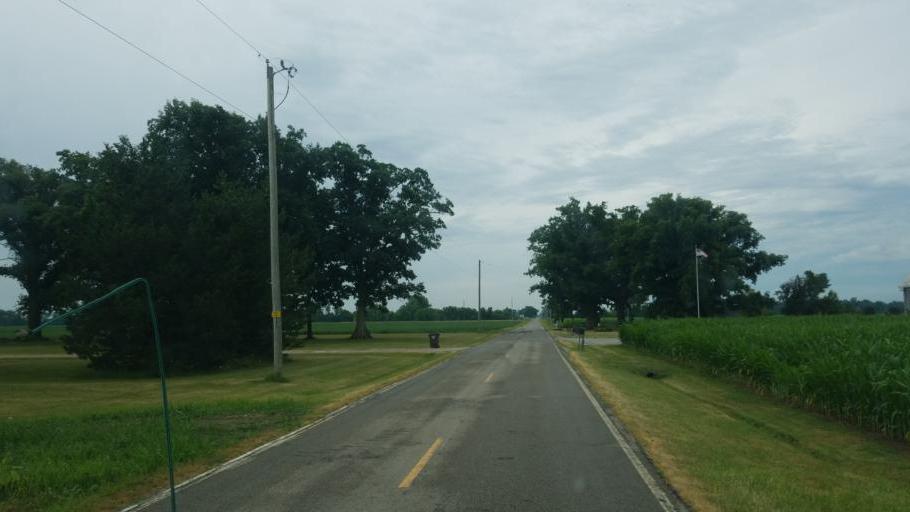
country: US
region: Ohio
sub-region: Defiance County
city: Hicksville
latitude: 41.2859
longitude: -84.6895
